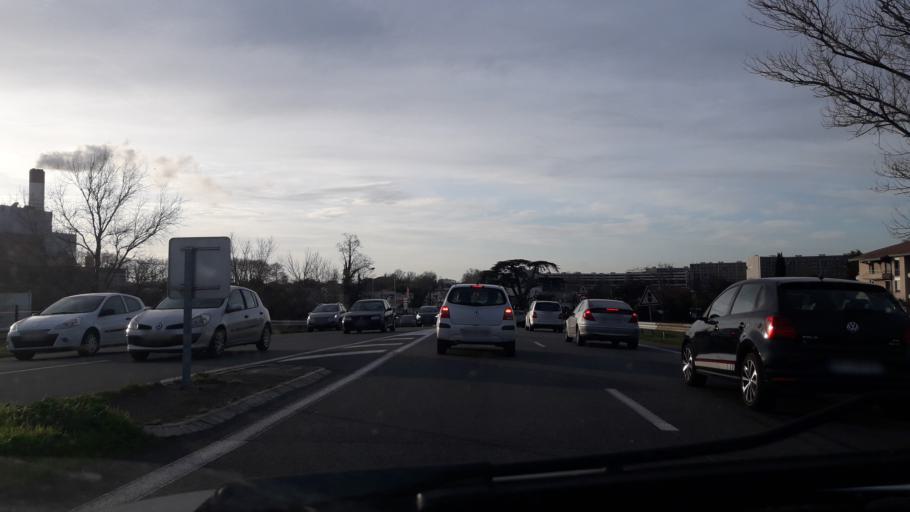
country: FR
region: Midi-Pyrenees
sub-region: Departement de la Haute-Garonne
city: Portet-sur-Garonne
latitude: 43.5575
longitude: 1.4043
